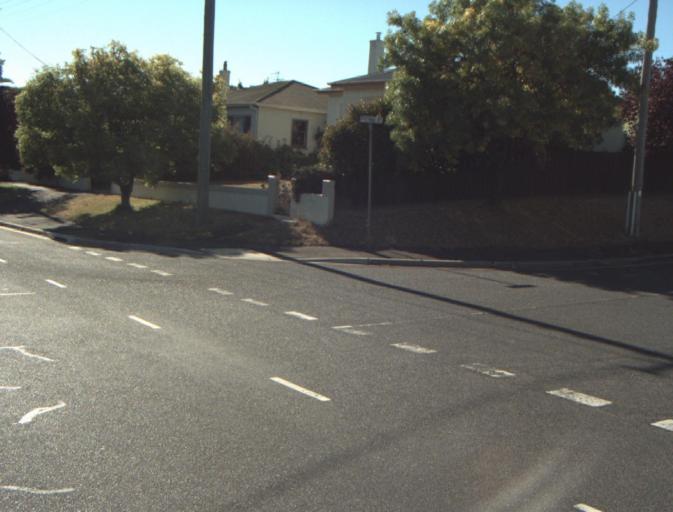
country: AU
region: Tasmania
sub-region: Launceston
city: East Launceston
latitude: -41.4597
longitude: 147.1569
